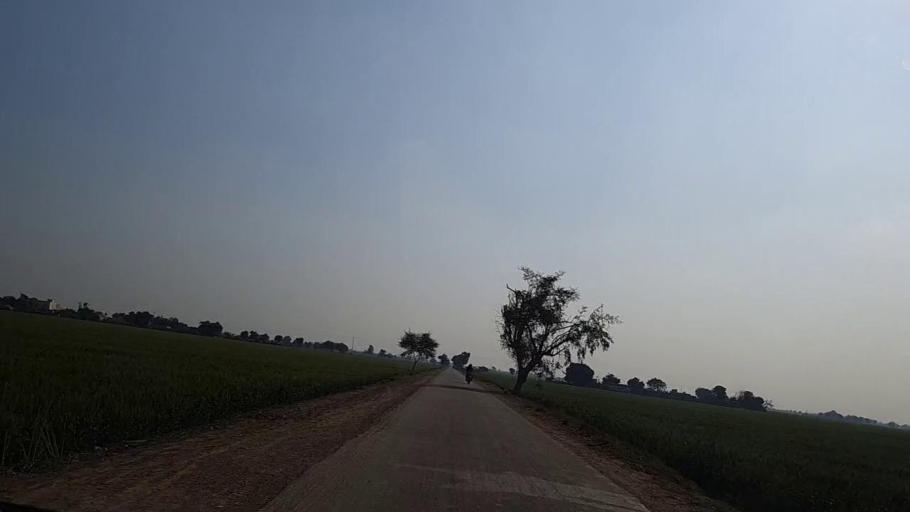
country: PK
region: Sindh
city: Sakrand
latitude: 26.0965
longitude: 68.2905
